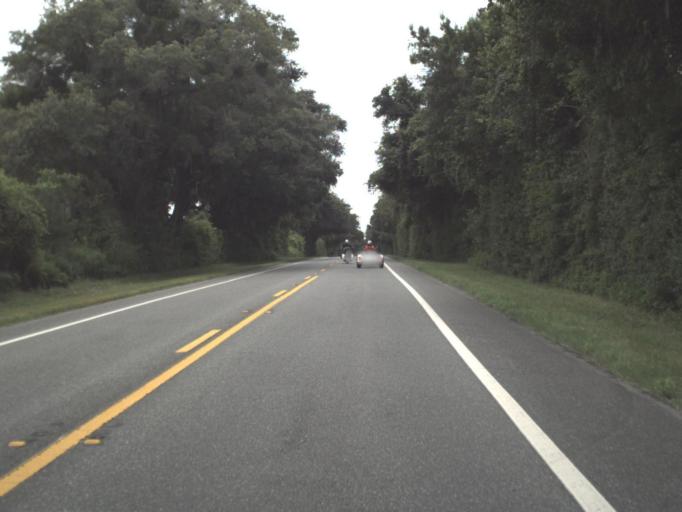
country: US
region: Florida
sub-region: Alachua County
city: Archer
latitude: 29.5732
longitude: -82.5455
